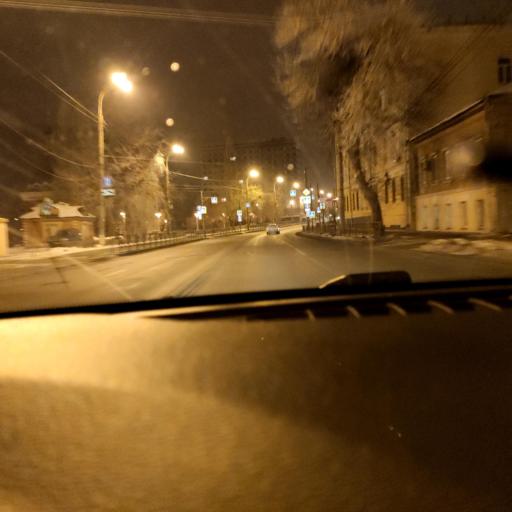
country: RU
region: Samara
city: Rozhdestveno
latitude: 53.1846
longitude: 50.0768
